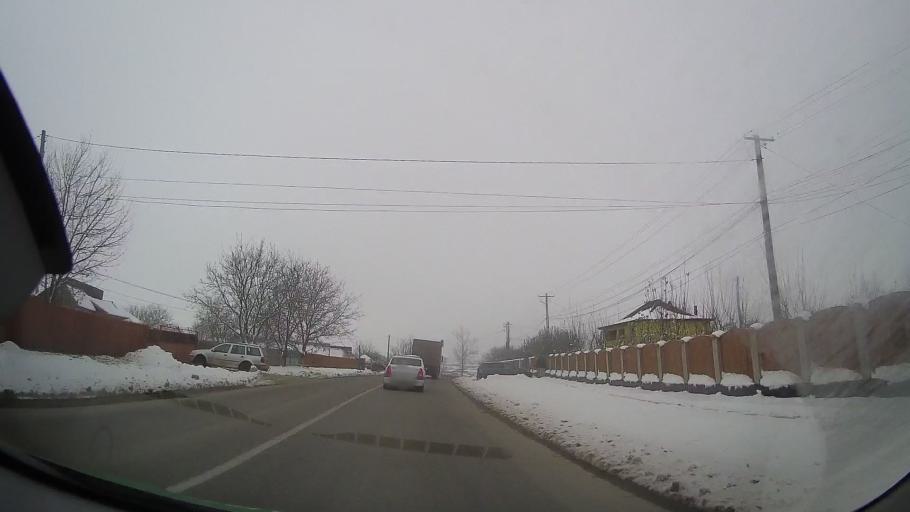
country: RO
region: Vaslui
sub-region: Comuna Todiresti
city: Todiresti
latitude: 46.8413
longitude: 27.3903
